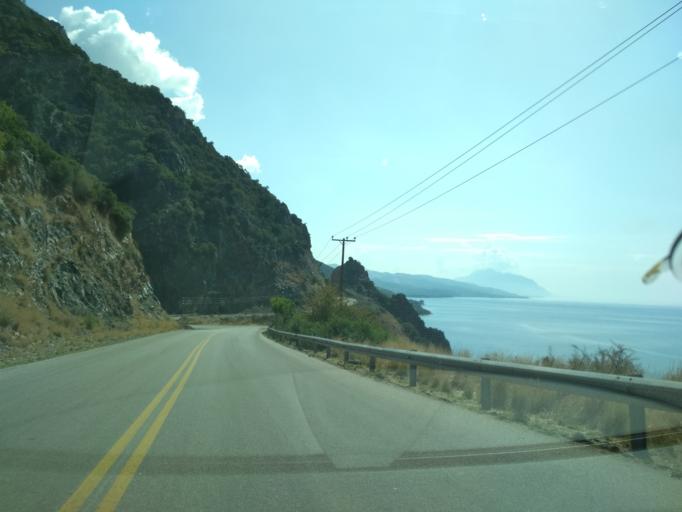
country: GR
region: Central Greece
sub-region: Nomos Evvoias
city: Roviai
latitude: 38.8481
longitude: 23.1539
